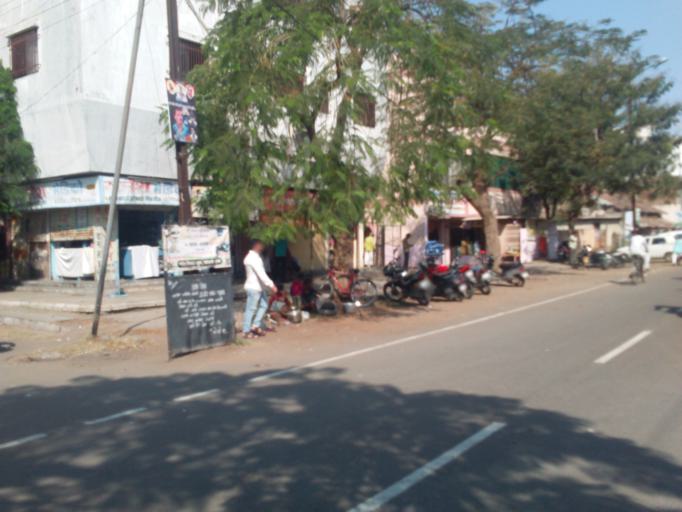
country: IN
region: Maharashtra
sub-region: Solapur
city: Solapur
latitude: 17.6646
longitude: 75.8978
